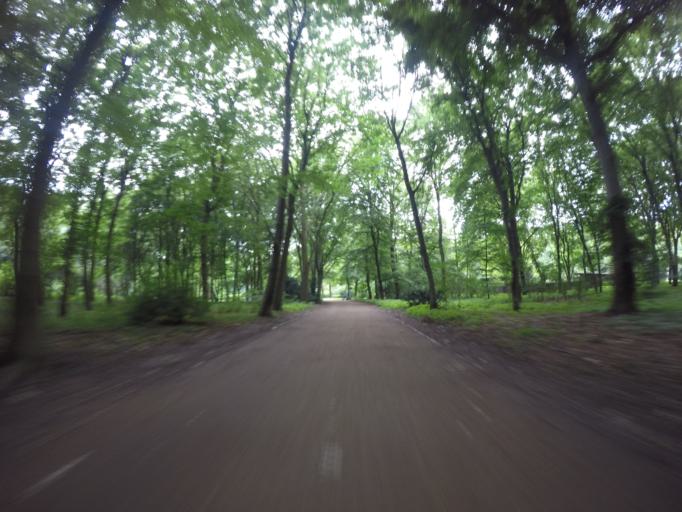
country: DE
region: Berlin
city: Tiergarten Bezirk
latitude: 52.5113
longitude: 13.3669
